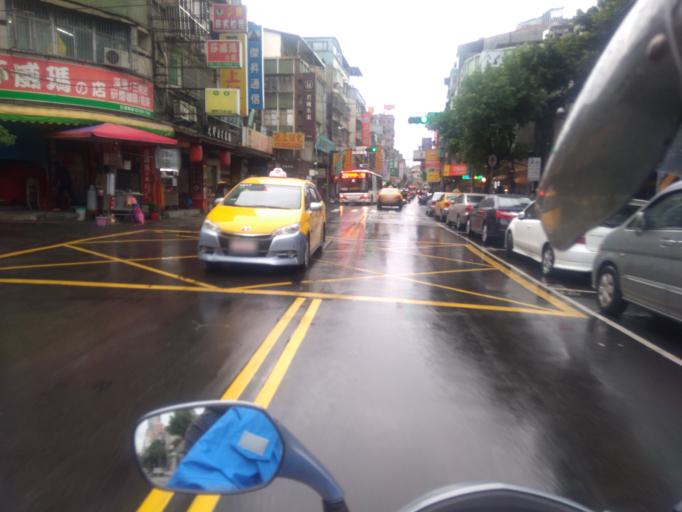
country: TW
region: Taipei
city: Taipei
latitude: 25.0846
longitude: 121.4908
